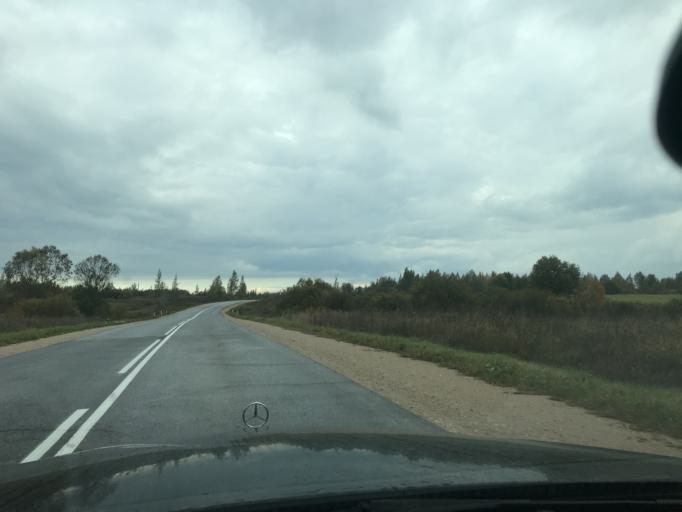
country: RU
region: Pskov
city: Izborsk
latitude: 57.6277
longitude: 27.9118
